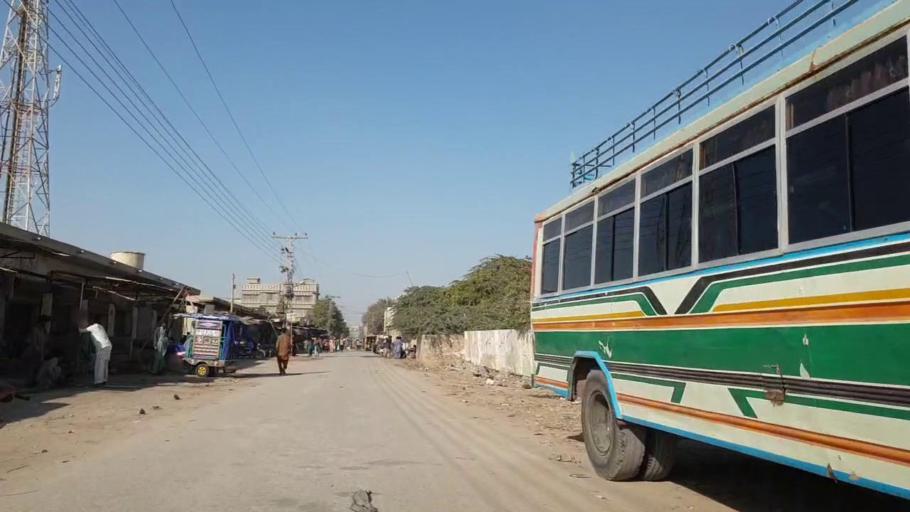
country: PK
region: Sindh
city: Digri
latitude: 25.1515
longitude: 69.1116
